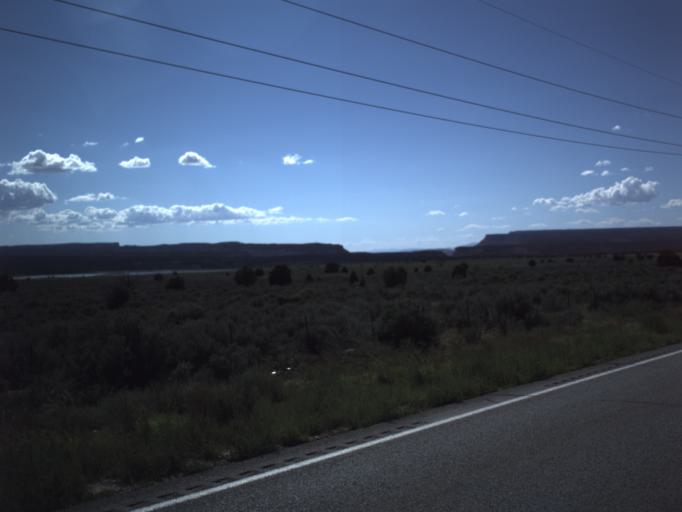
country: US
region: Arizona
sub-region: Mohave County
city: Colorado City
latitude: 37.0098
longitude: -113.0140
